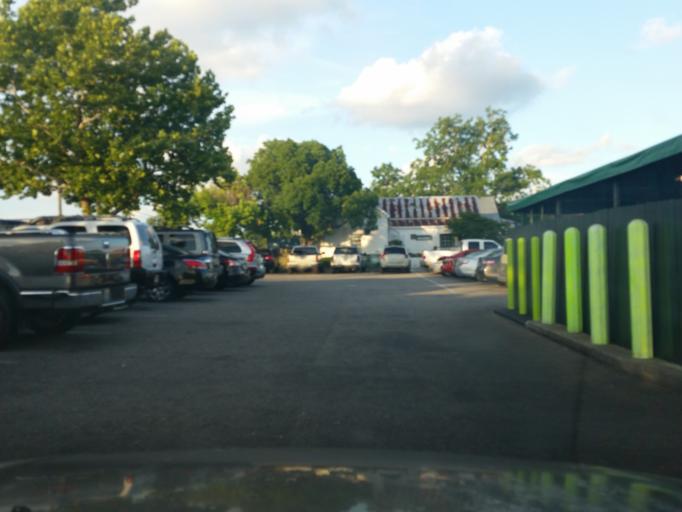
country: US
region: Florida
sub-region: Escambia County
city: Pensacola
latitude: 30.4183
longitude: -87.2025
